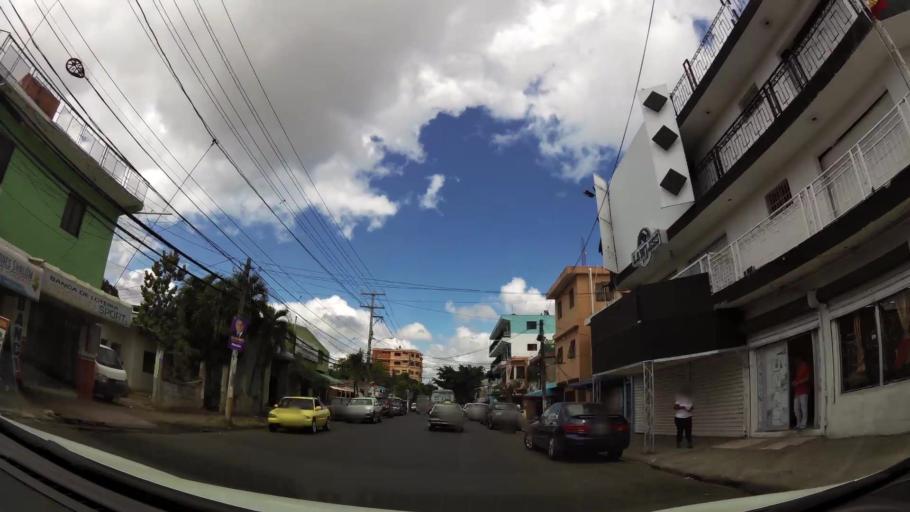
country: DO
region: Nacional
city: Ensanche Luperon
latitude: 18.5032
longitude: -69.8956
